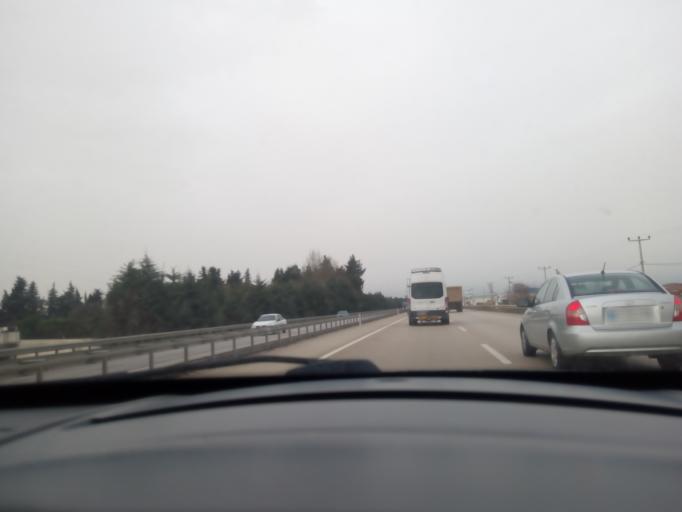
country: TR
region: Bursa
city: Tatkavakli
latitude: 40.0319
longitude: 28.3533
